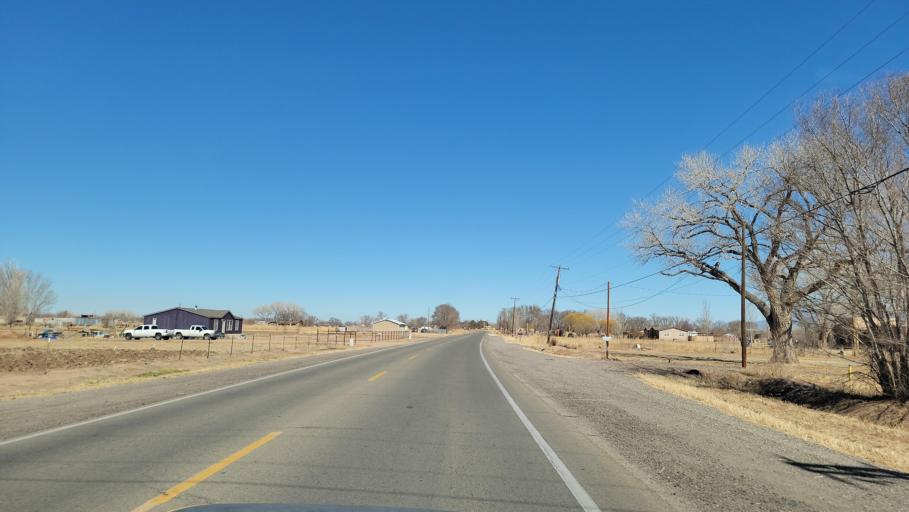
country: US
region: New Mexico
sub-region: Bernalillo County
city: South Valley
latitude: 34.9332
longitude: -106.6923
